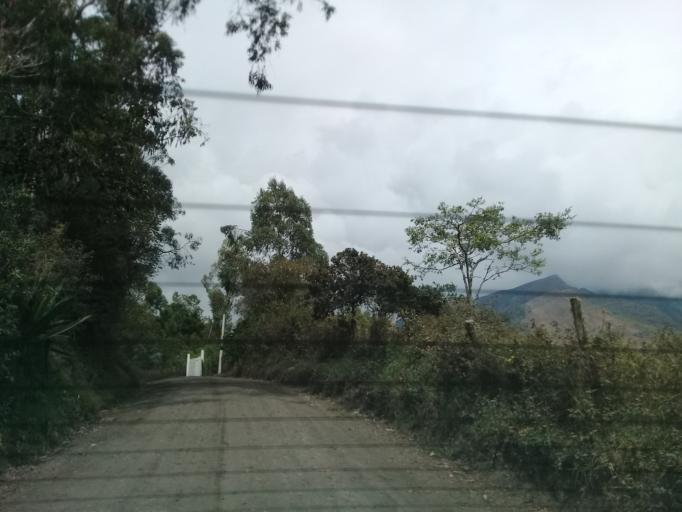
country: CO
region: Cundinamarca
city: Caqueza
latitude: 4.4126
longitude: -73.9840
